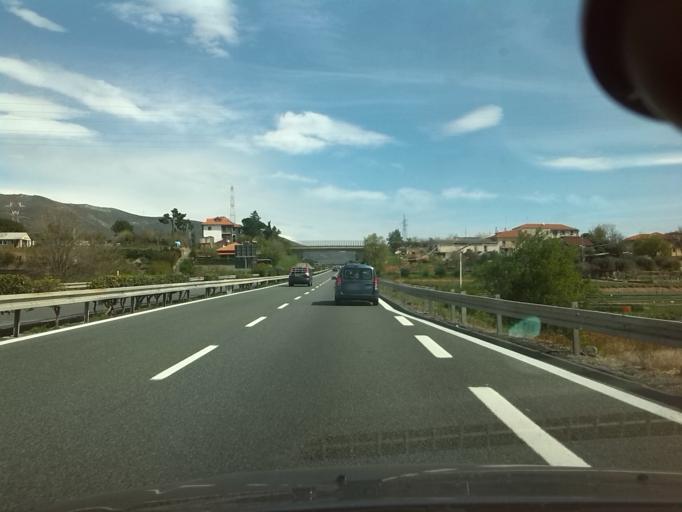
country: IT
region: Liguria
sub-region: Provincia di Savona
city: Campochiesa
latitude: 44.0673
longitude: 8.1767
